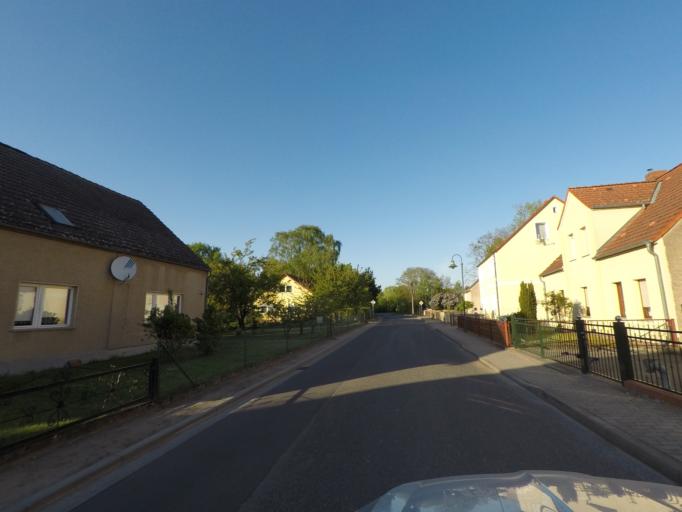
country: DE
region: Brandenburg
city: Oderberg
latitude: 52.8381
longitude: 14.0085
